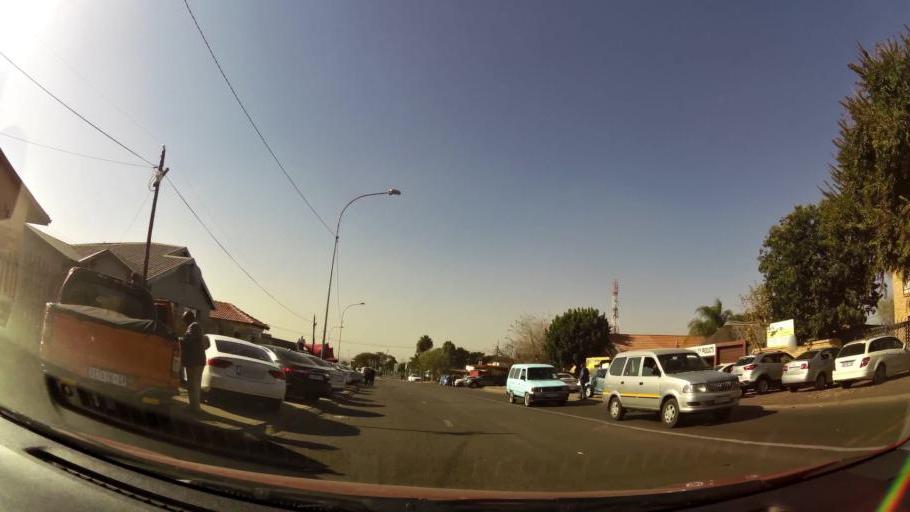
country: ZA
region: Gauteng
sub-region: City of Tshwane Metropolitan Municipality
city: Mabopane
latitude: -25.5281
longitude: 28.1083
